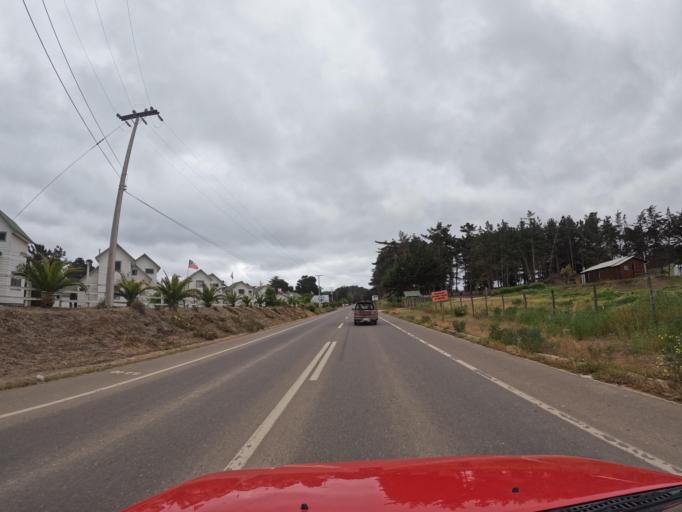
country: CL
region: O'Higgins
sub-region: Provincia de Colchagua
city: Santa Cruz
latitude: -34.4545
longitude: -72.0276
